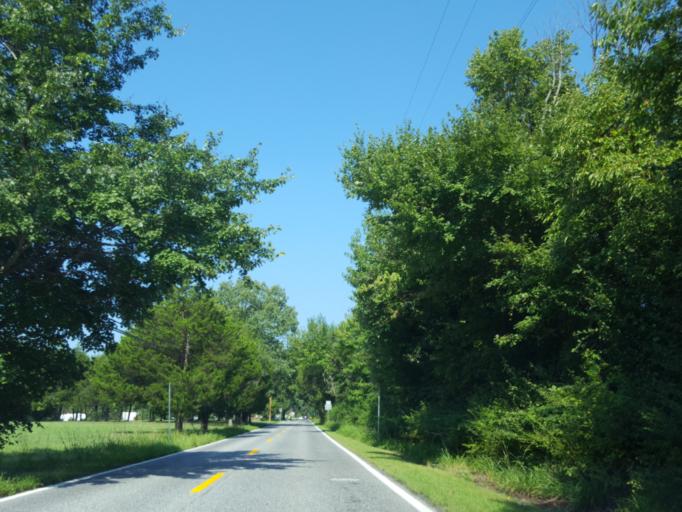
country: US
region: Maryland
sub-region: Anne Arundel County
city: Shady Side
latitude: 38.8478
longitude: -76.5528
